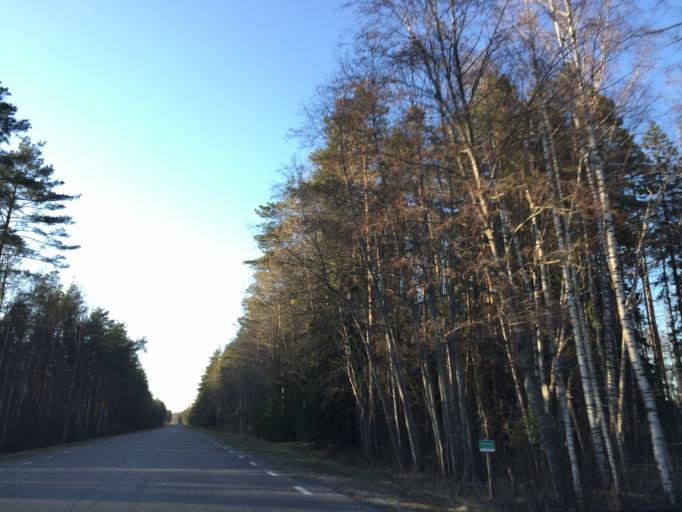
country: EE
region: Ida-Virumaa
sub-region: Toila vald
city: Voka
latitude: 59.1007
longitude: 27.6495
